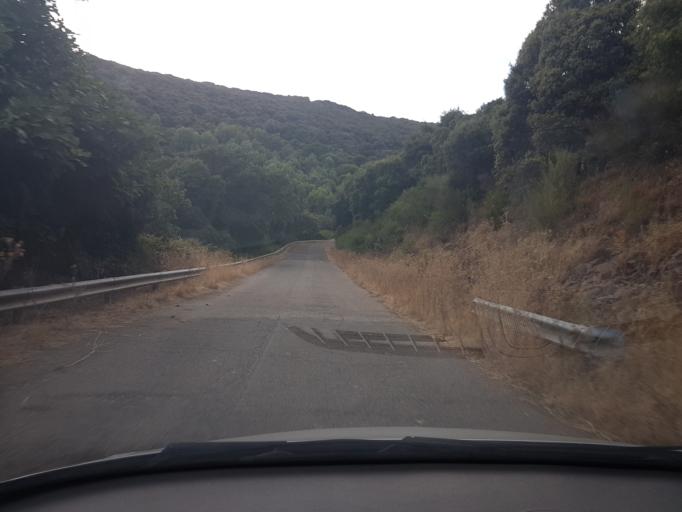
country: IT
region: Sardinia
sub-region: Provincia di Oristano
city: Seneghe
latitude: 40.1117
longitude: 8.6150
